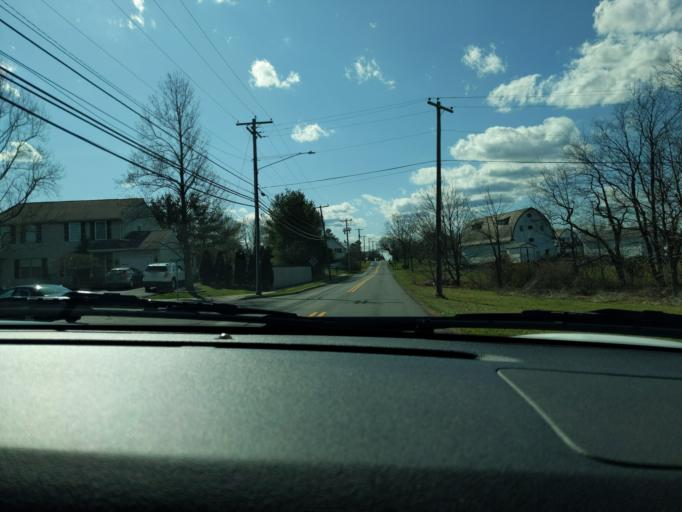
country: US
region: Pennsylvania
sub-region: Bucks County
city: Spinnerstown
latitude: 40.4362
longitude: -75.4030
